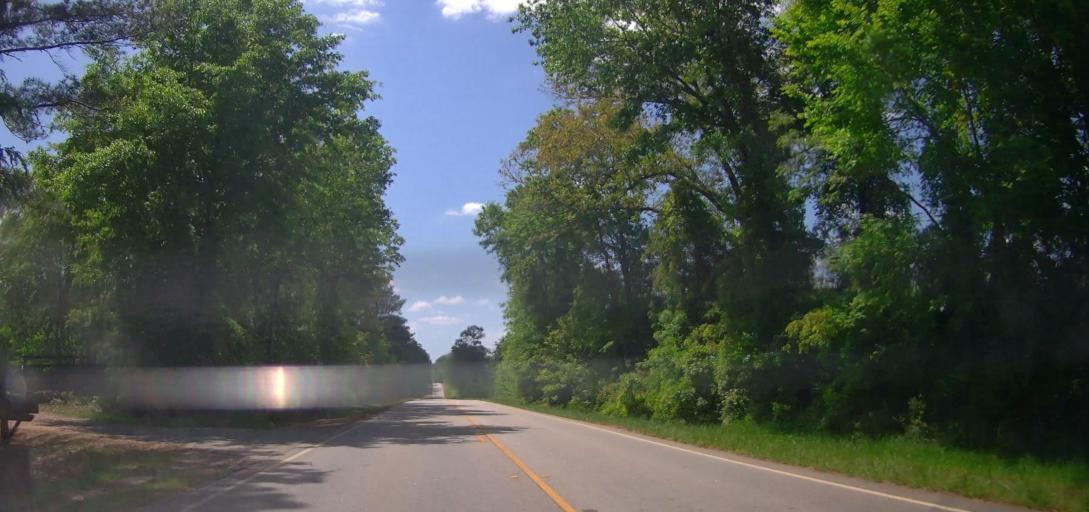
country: US
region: Georgia
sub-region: Putnam County
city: Eatonton
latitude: 33.3392
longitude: -83.3332
